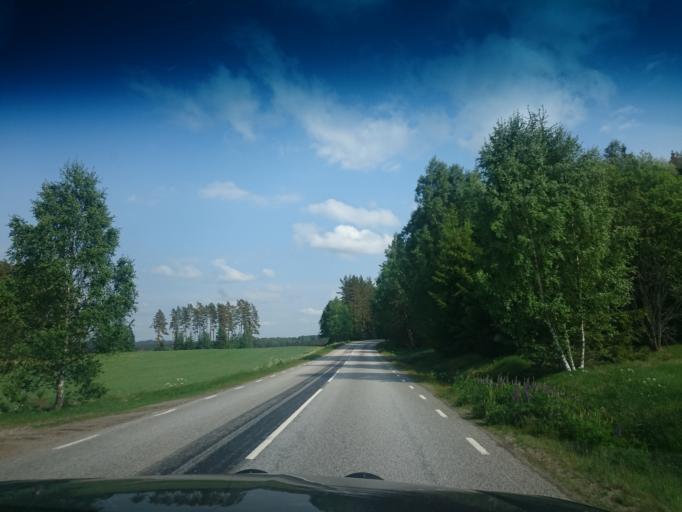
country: SE
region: Joenkoeping
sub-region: Vetlanda Kommun
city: Vetlanda
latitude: 57.3739
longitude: 15.0486
